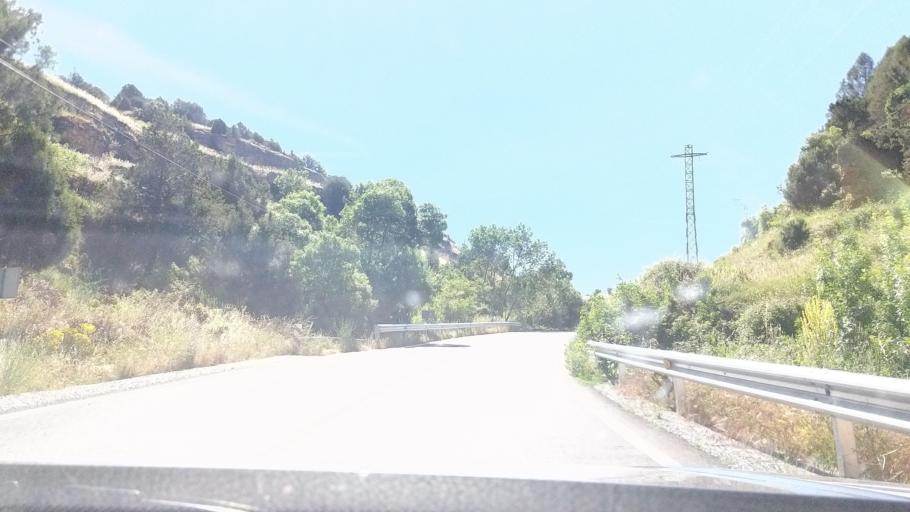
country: ES
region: Castille and Leon
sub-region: Provincia de Segovia
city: Pedraza
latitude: 41.1330
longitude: -3.8110
